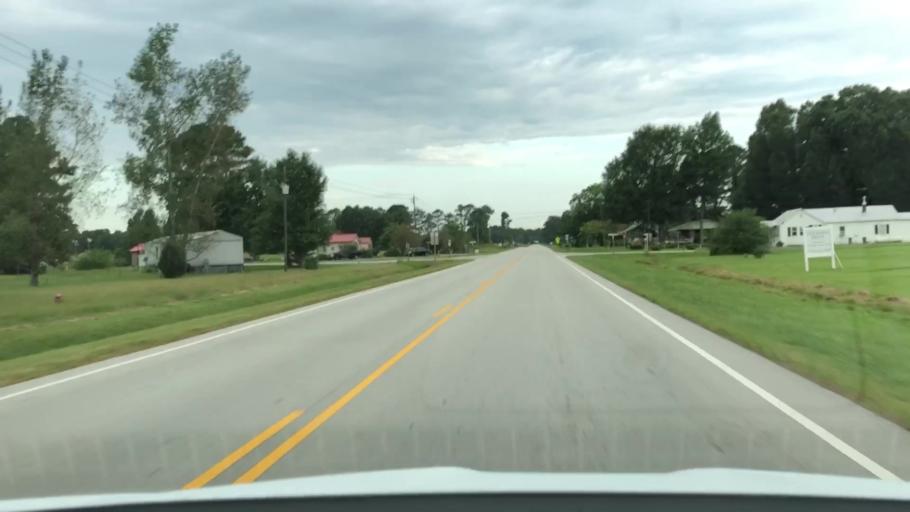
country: US
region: North Carolina
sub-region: Jones County
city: Trenton
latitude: 35.0341
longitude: -77.3270
